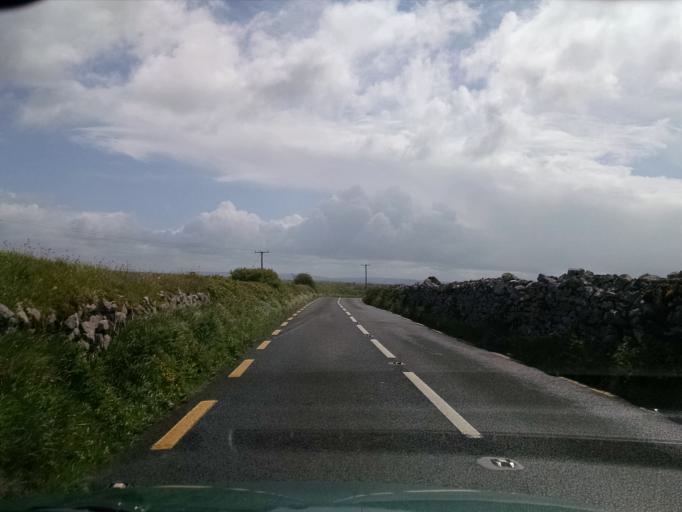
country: IE
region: Connaught
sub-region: County Galway
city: Gaillimh
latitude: 53.1453
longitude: -9.0378
